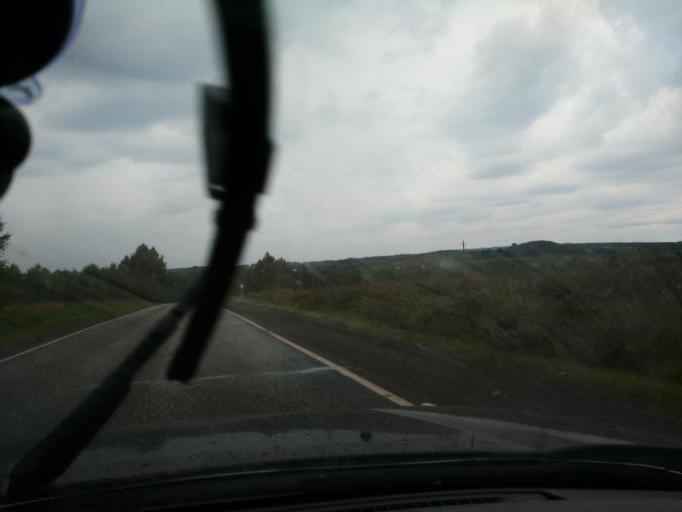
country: RU
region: Perm
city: Barda
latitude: 56.8502
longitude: 55.9483
